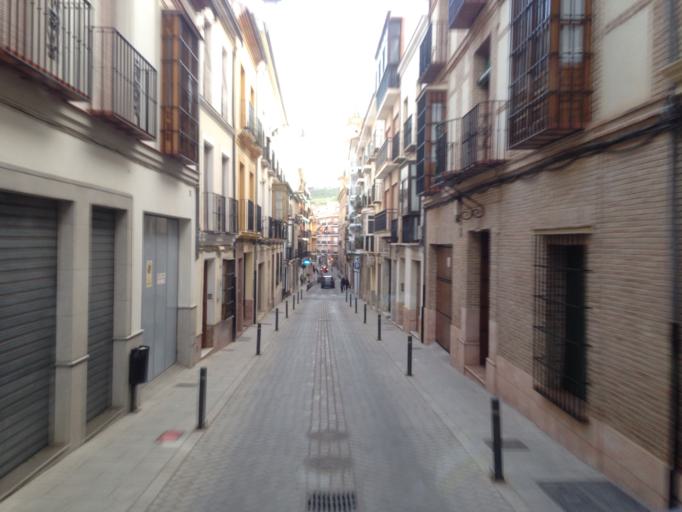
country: ES
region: Andalusia
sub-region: Provincia de Malaga
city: Antequera
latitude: 37.0212
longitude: -4.5596
